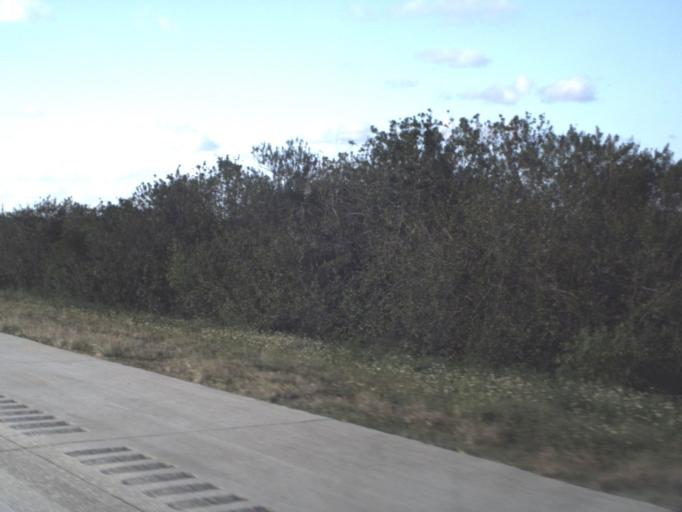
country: US
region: Florida
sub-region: Brevard County
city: Cocoa West
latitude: 28.3160
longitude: -80.7657
